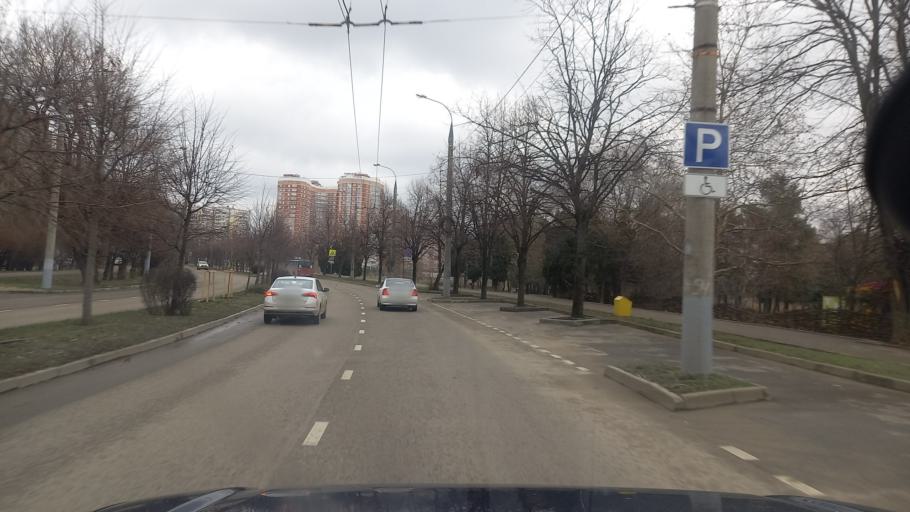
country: RU
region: Krasnodarskiy
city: Pashkovskiy
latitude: 45.0338
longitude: 39.1014
